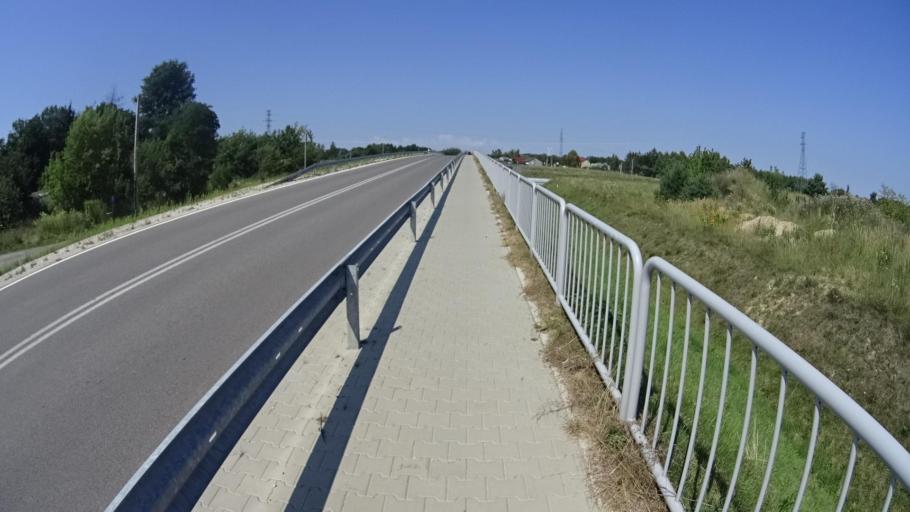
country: PL
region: Masovian Voivodeship
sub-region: Powiat piaseczynski
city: Tarczyn
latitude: 51.9563
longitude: 20.8530
